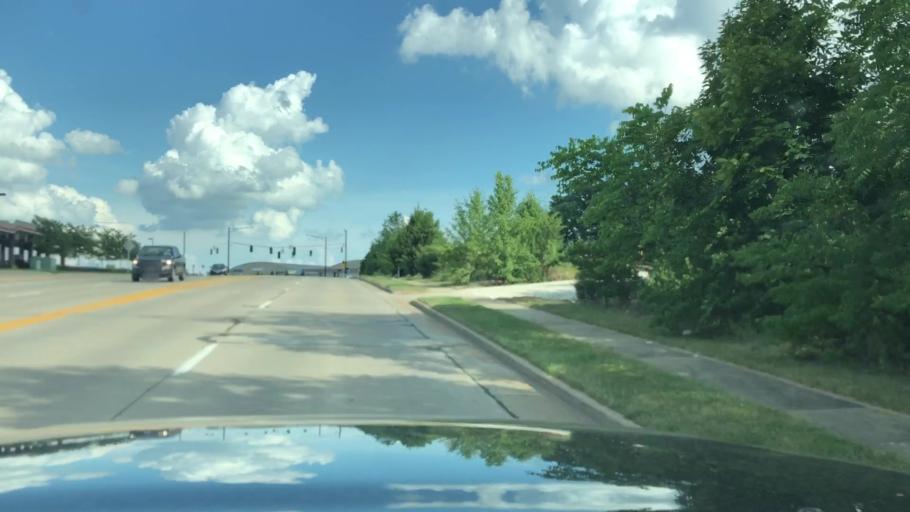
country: US
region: Missouri
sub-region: Saint Charles County
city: Wentzville
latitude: 38.8233
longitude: -90.8544
